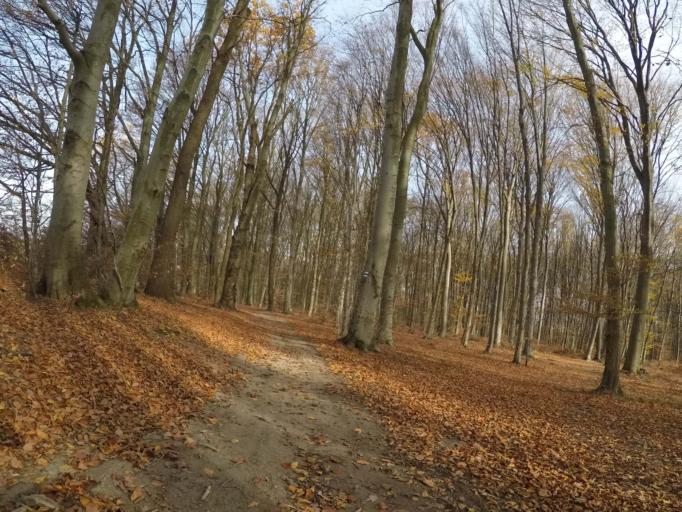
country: SK
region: Presovsky
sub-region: Okres Presov
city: Presov
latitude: 48.9178
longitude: 21.2195
